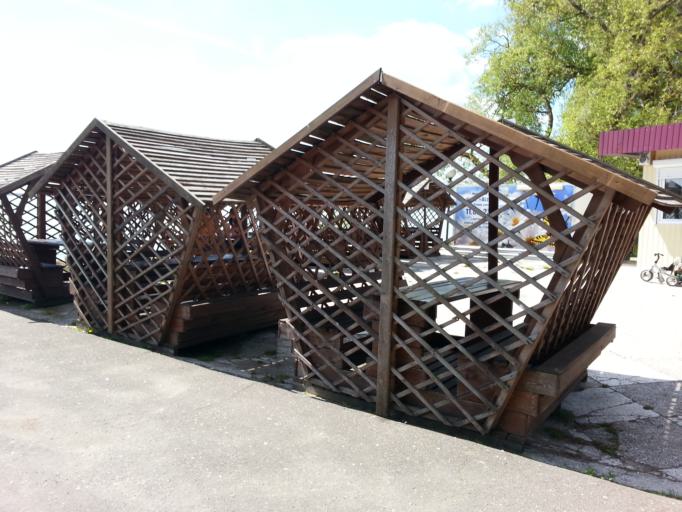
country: BY
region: Minsk
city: Narach
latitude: 54.9066
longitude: 26.7072
